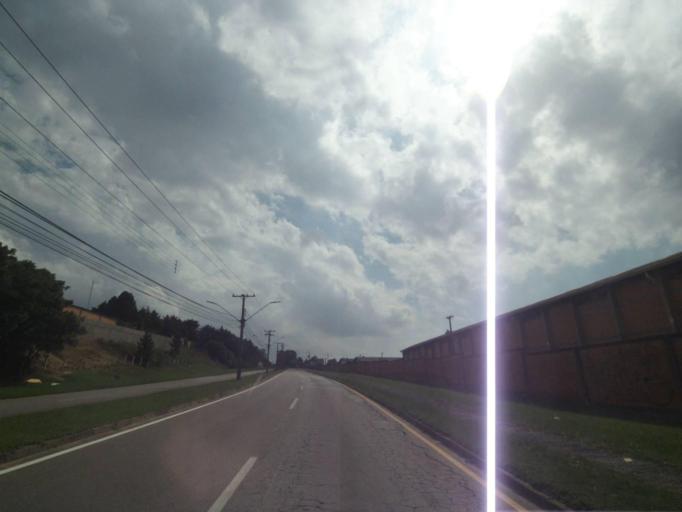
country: BR
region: Parana
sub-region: Araucaria
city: Araucaria
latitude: -25.5174
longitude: -49.3428
